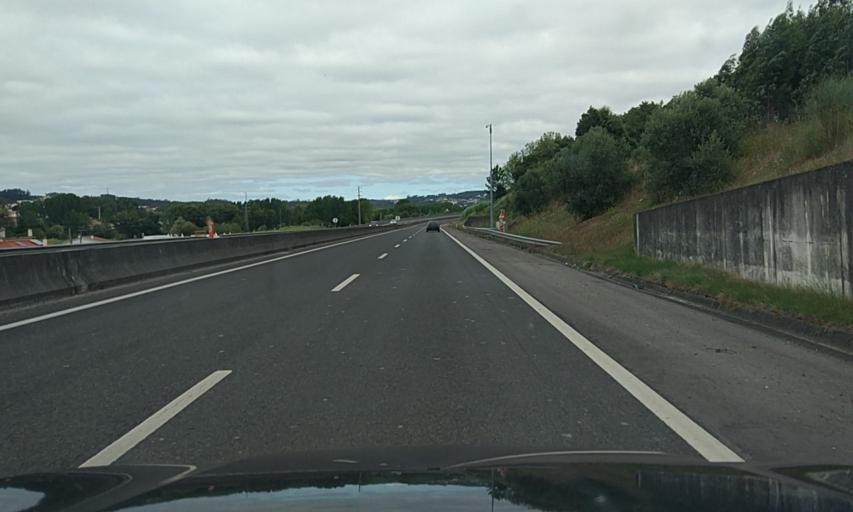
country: PT
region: Leiria
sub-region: Leiria
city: Leiria
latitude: 39.7450
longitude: -8.7841
